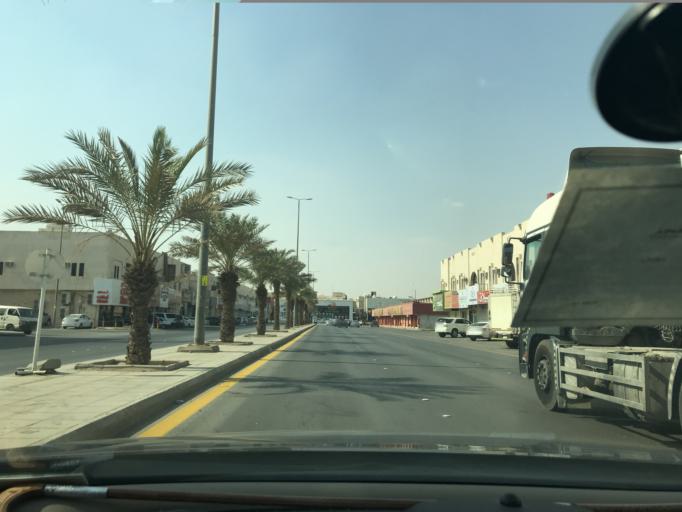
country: SA
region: Ar Riyad
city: Riyadh
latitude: 24.7428
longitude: 46.7573
